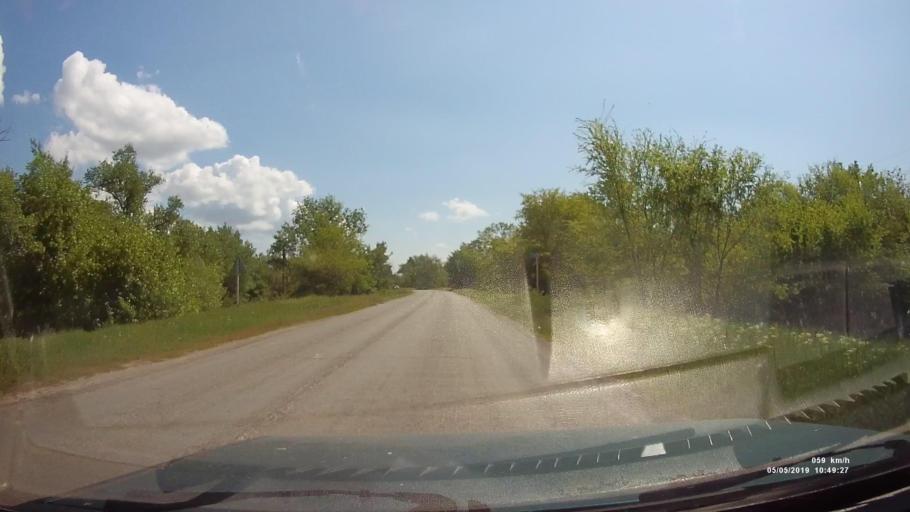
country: RU
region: Rostov
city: Ust'-Donetskiy
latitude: 47.6462
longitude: 40.8144
